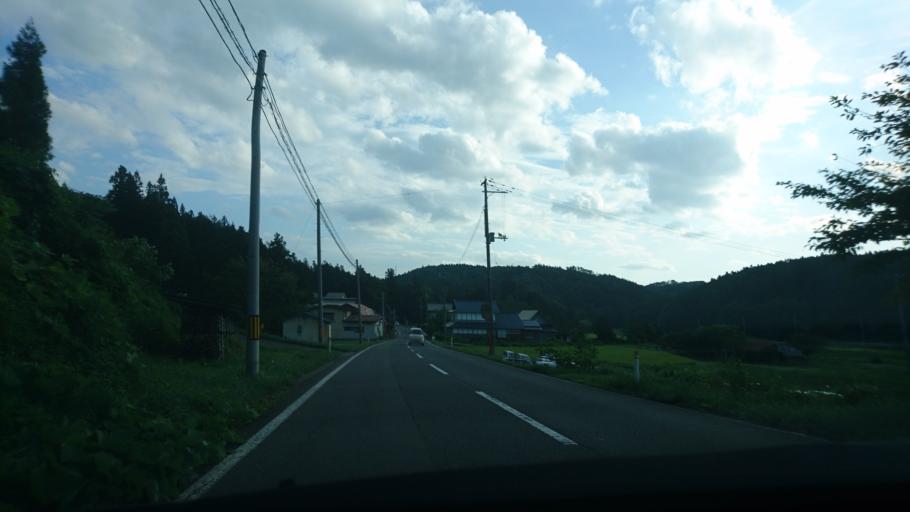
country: JP
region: Iwate
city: Ichinoseki
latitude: 39.0210
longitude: 141.2905
